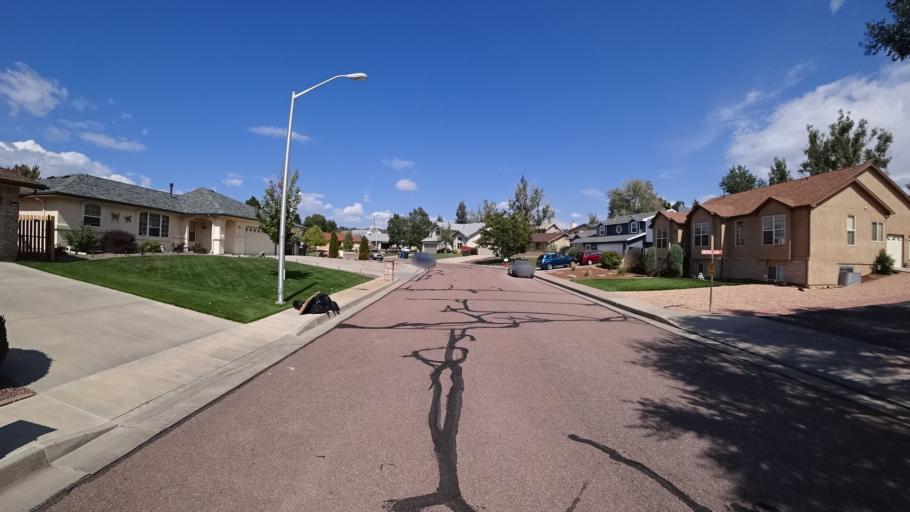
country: US
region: Colorado
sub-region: El Paso County
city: Cimarron Hills
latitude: 38.8634
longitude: -104.7272
